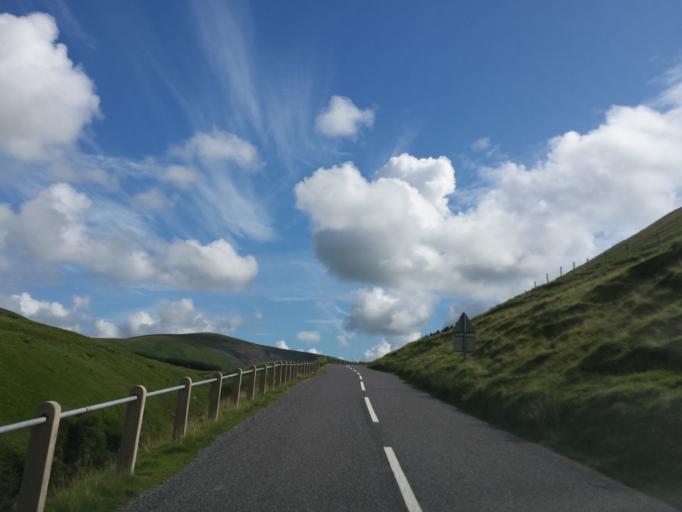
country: GB
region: Scotland
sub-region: Dumfries and Galloway
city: Moffat
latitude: 55.4272
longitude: -3.2690
